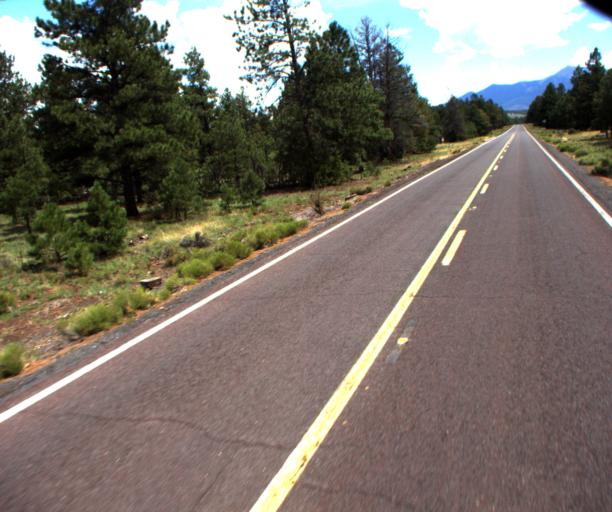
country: US
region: Arizona
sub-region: Coconino County
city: Parks
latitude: 35.4692
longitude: -111.7881
